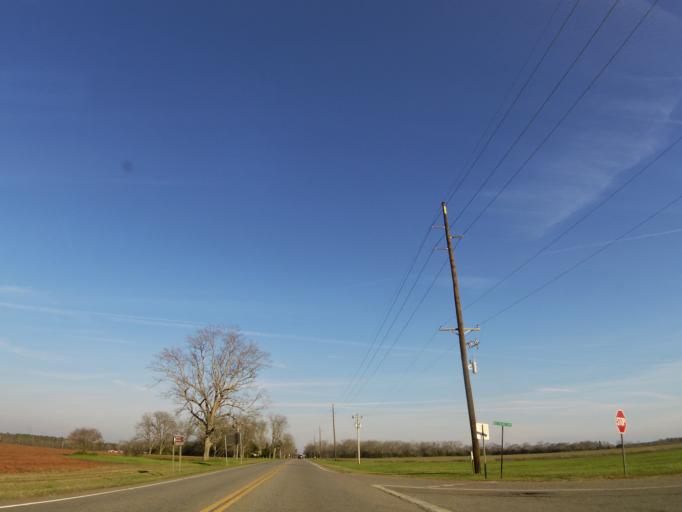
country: US
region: Georgia
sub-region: Webster County
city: Preston
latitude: 32.0342
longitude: -84.4118
